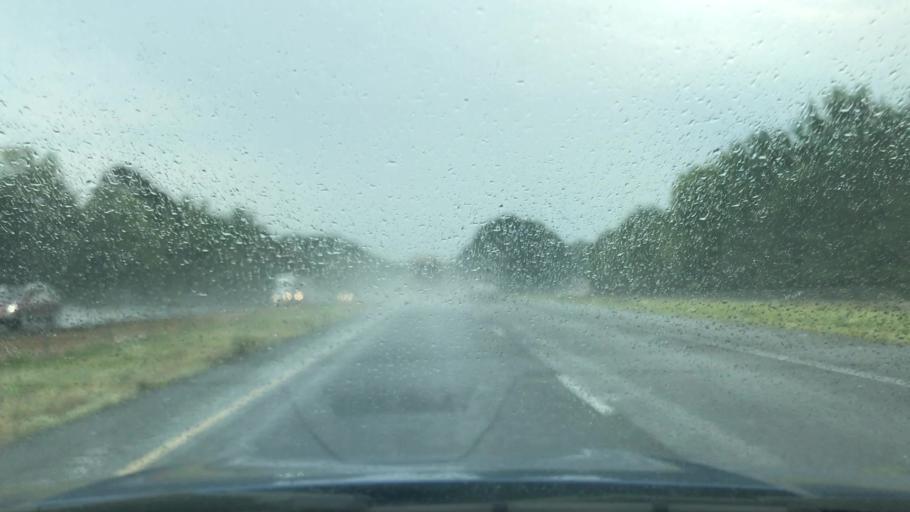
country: US
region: Texas
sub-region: Harrison County
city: Marshall
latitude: 32.4950
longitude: -94.2186
